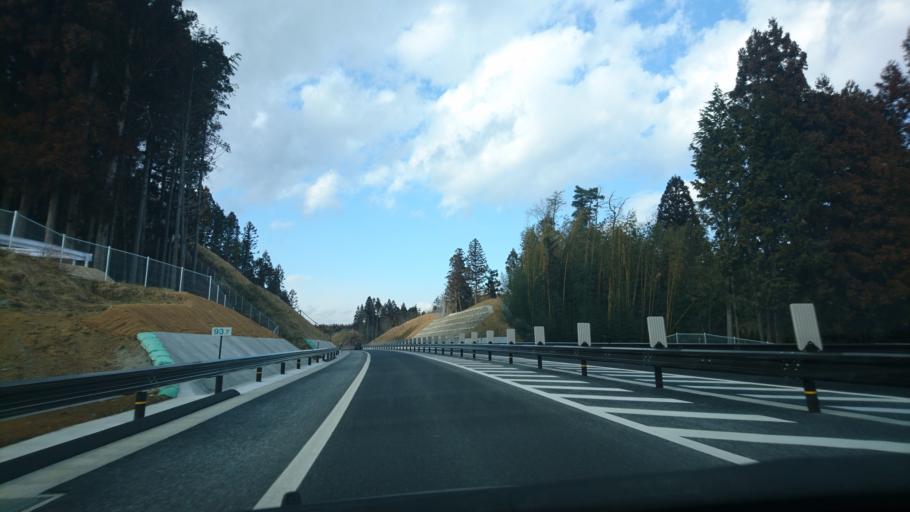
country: JP
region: Miyagi
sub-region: Oshika Gun
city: Onagawa Cho
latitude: 38.7429
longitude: 141.5236
